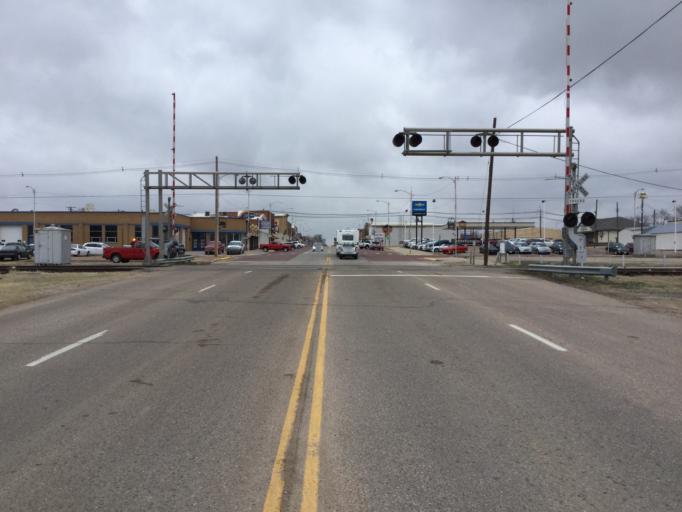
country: US
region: Kansas
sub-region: Barton County
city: Hoisington
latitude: 38.5109
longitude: -98.7774
